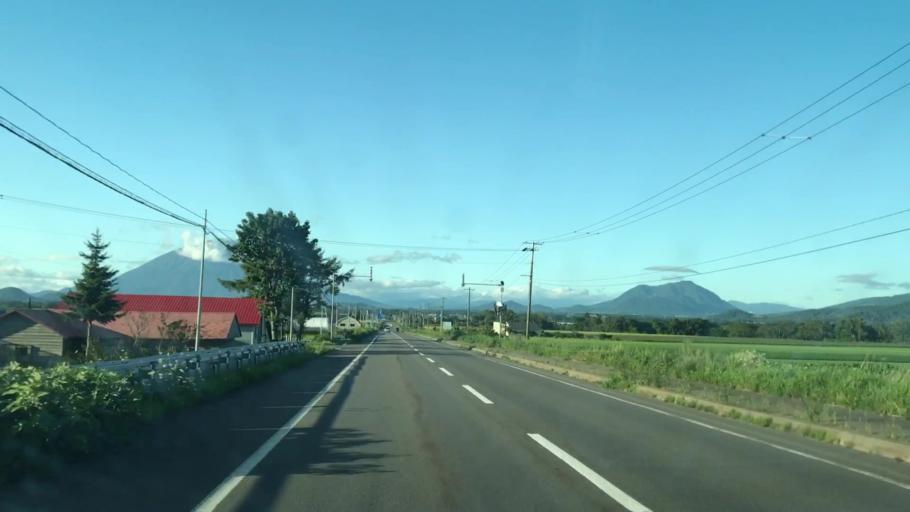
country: JP
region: Hokkaido
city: Date
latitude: 42.6365
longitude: 140.8018
